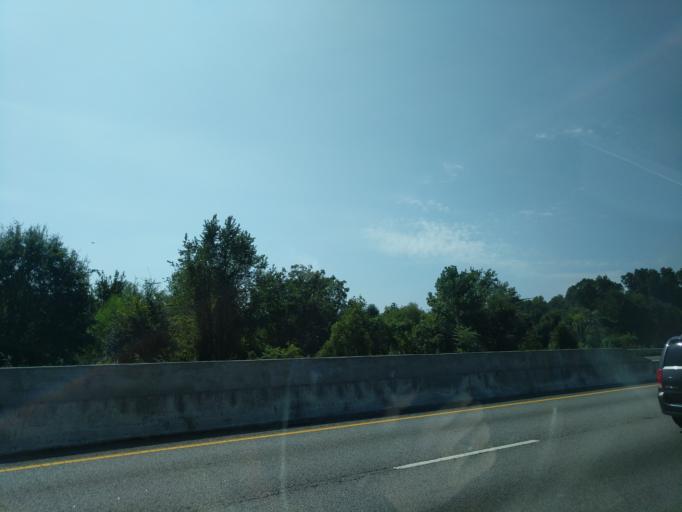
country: US
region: South Carolina
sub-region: Greenville County
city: Five Forks
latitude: 34.8562
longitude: -82.2680
